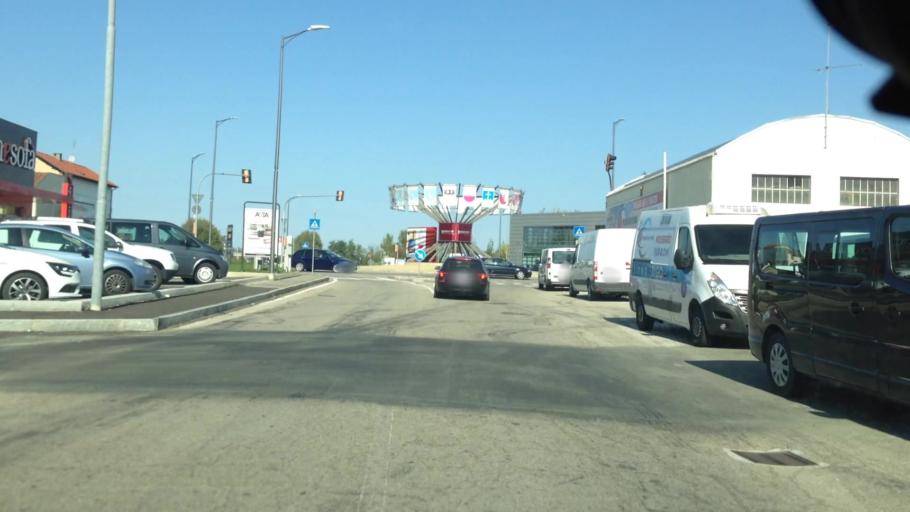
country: IT
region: Piedmont
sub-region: Provincia di Asti
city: Asti
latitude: 44.9051
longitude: 8.2316
